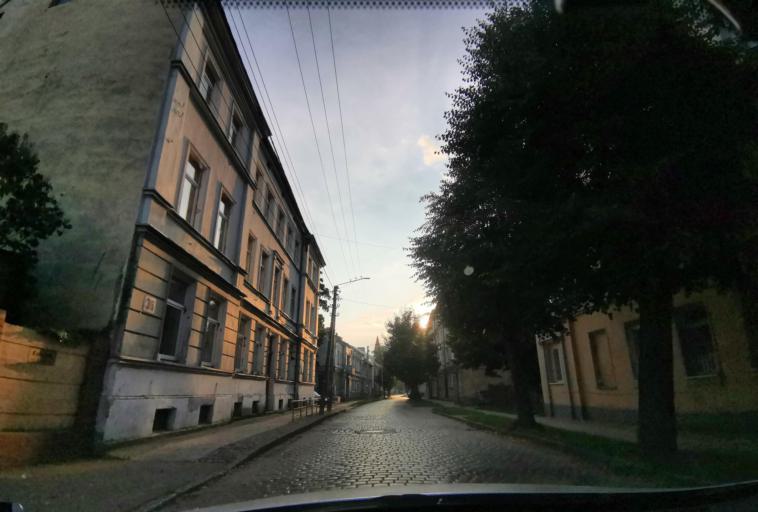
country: RU
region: Kaliningrad
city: Sovetsk
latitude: 55.0791
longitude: 21.9014
